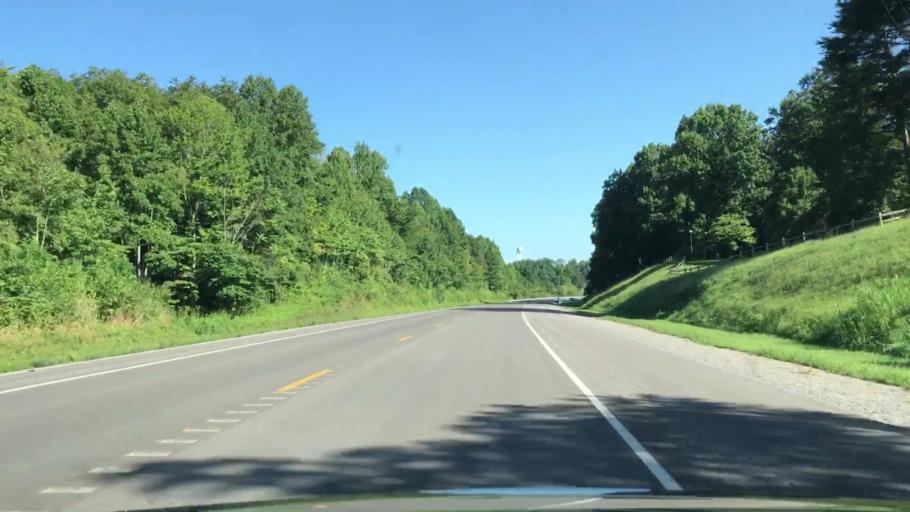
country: US
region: Kentucky
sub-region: Cumberland County
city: Burkesville
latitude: 36.6835
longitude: -85.3737
